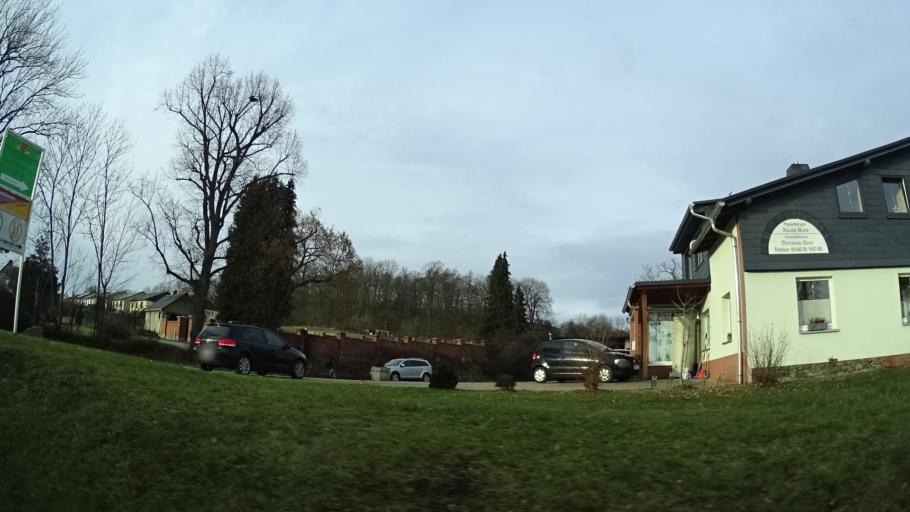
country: DE
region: Thuringia
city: Tegau
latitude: 50.6473
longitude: 11.8983
